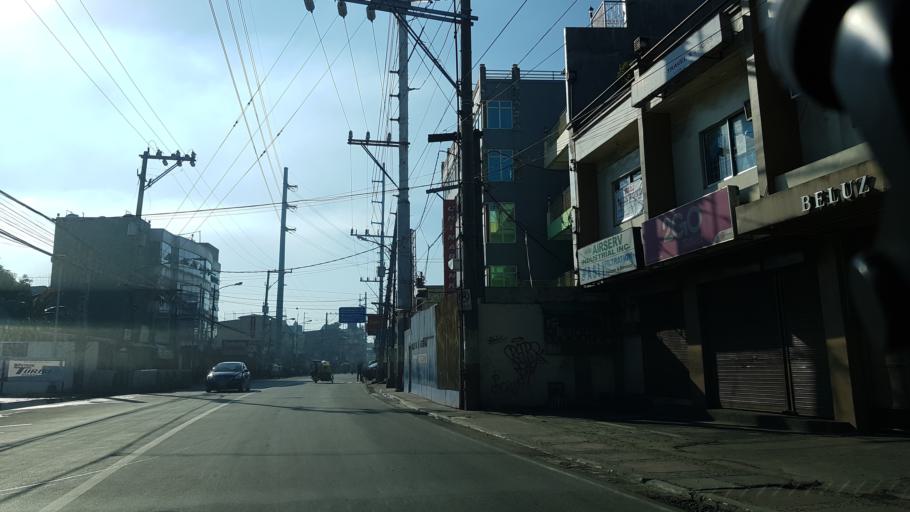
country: PH
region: Calabarzon
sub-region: Province of Rizal
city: Pateros
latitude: 14.5529
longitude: 121.0728
